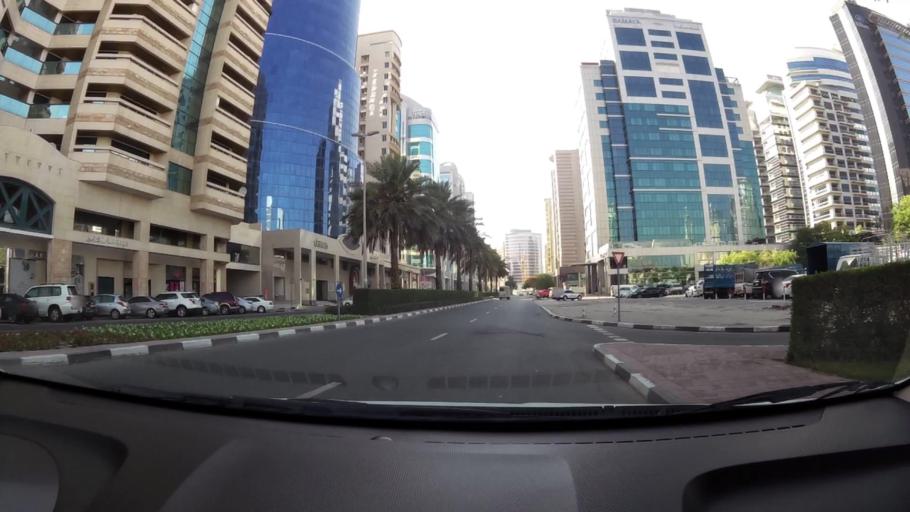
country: AE
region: Ash Shariqah
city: Sharjah
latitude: 25.2612
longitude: 55.3183
